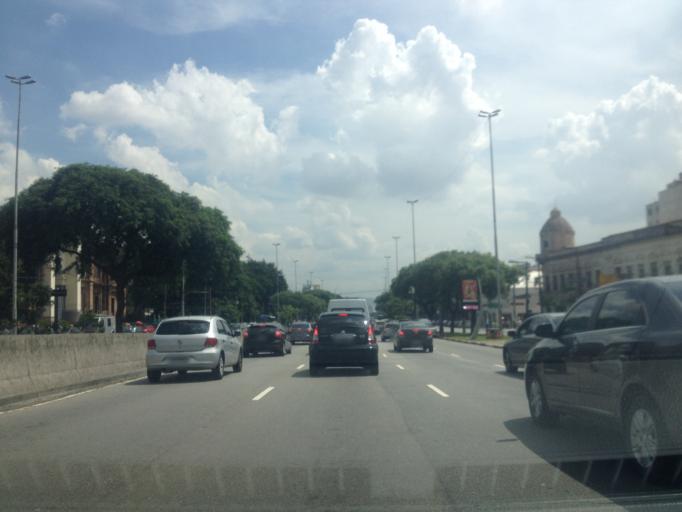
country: BR
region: Sao Paulo
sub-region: Sao Paulo
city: Sao Paulo
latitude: -23.5354
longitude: -46.6335
